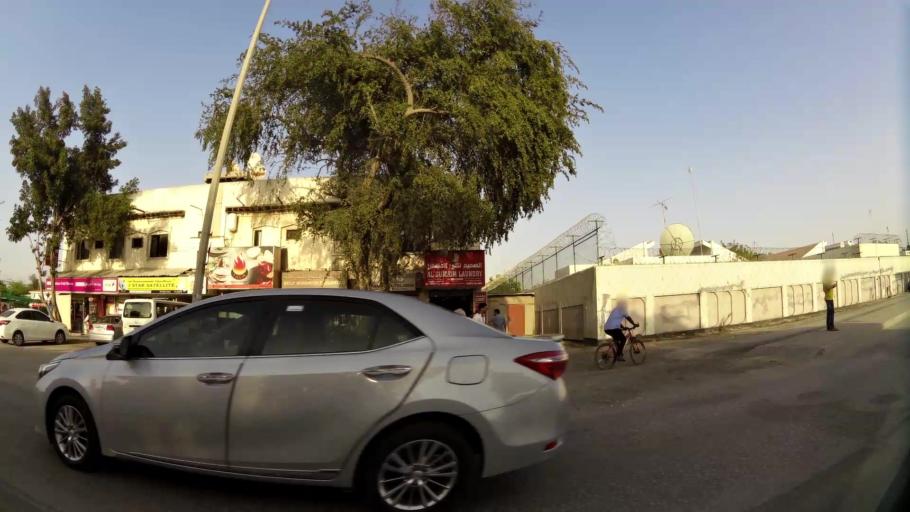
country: BH
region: Manama
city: Jidd Hafs
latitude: 26.1976
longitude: 50.4857
